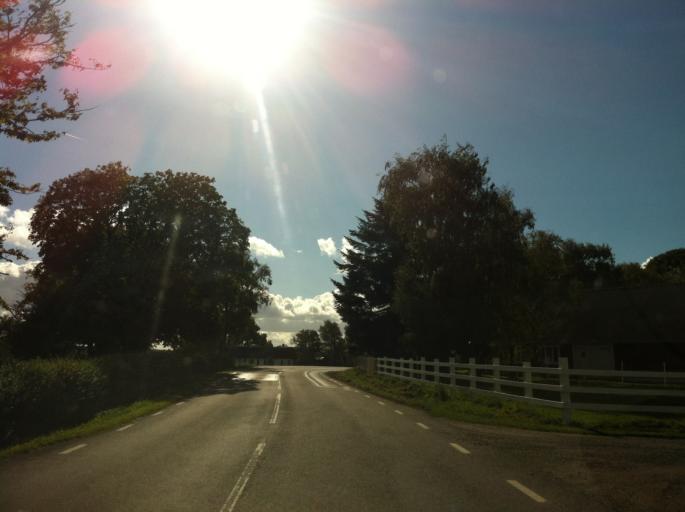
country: SE
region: Skane
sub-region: Sjobo Kommun
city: Sjoebo
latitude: 55.6504
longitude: 13.8093
